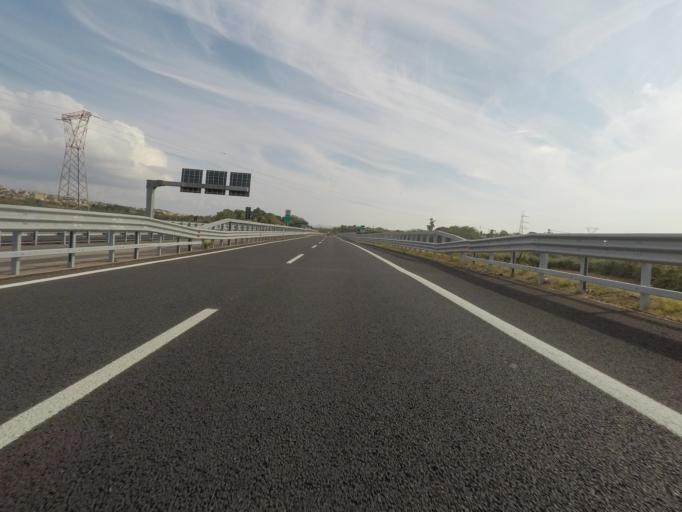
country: IT
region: Latium
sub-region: Provincia di Viterbo
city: Tarquinia
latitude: 42.2513
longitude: 11.7325
